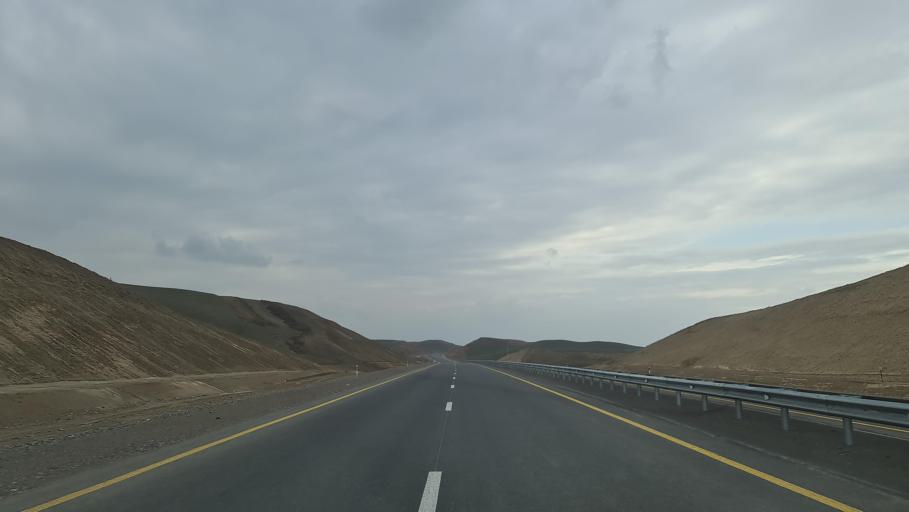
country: KZ
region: Almaty Oblysy
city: Burunday
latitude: 43.2962
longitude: 76.2107
